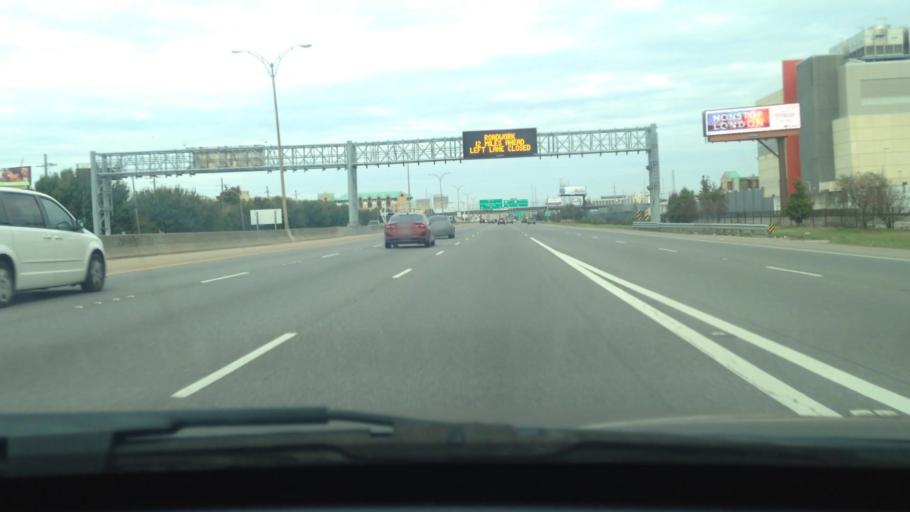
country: US
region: Louisiana
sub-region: Orleans Parish
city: New Orleans
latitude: 29.9592
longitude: -90.0960
